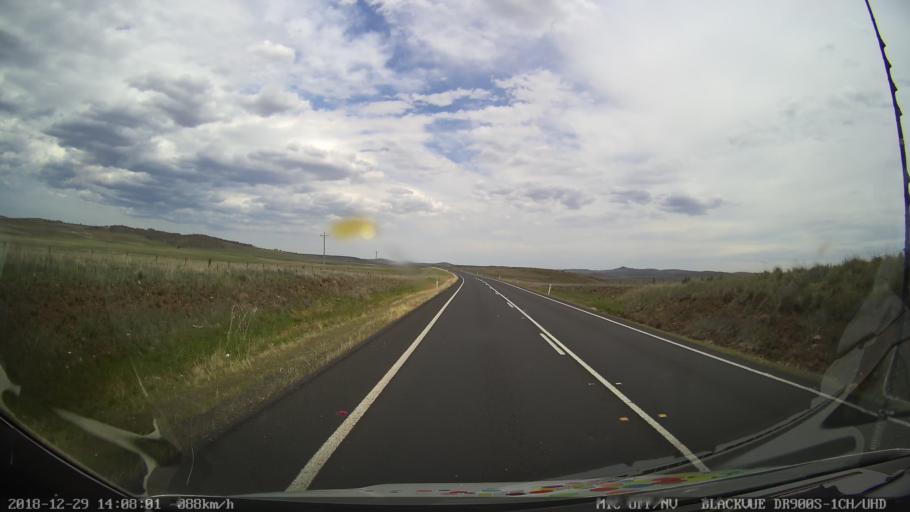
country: AU
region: New South Wales
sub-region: Cooma-Monaro
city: Cooma
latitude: -36.3595
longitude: 149.2144
